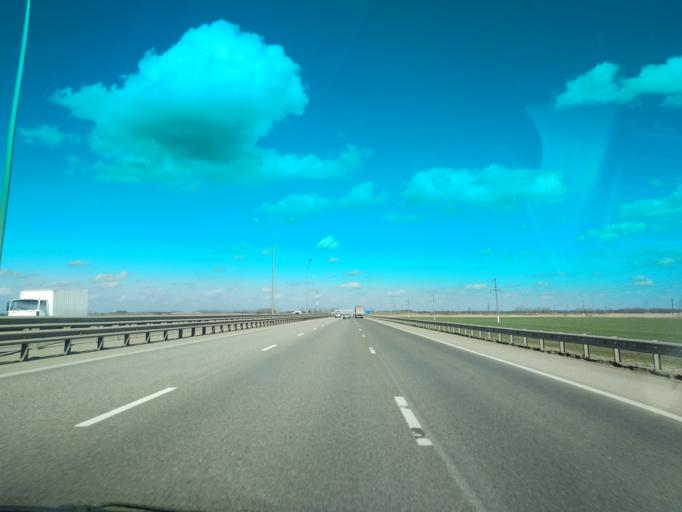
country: RU
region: Krasnodarskiy
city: Dinskaya
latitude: 45.2385
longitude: 39.1904
